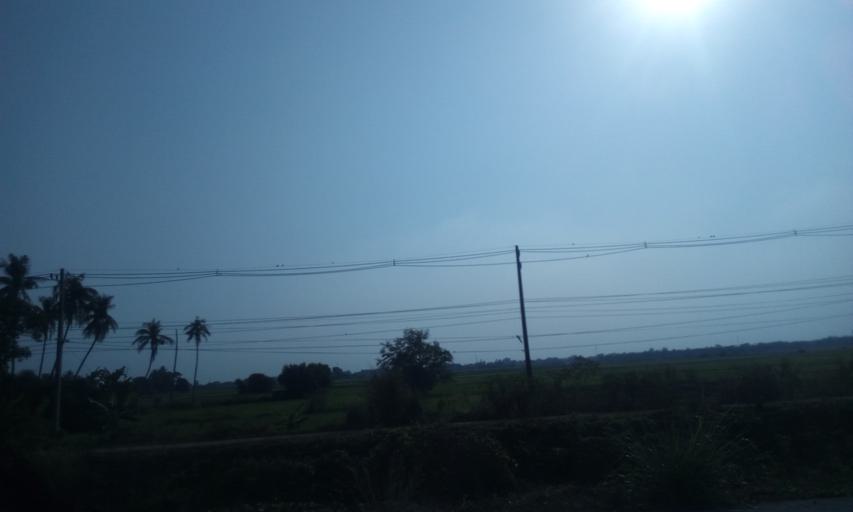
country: TH
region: Sing Buri
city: Sing Buri
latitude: 14.8419
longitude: 100.4318
